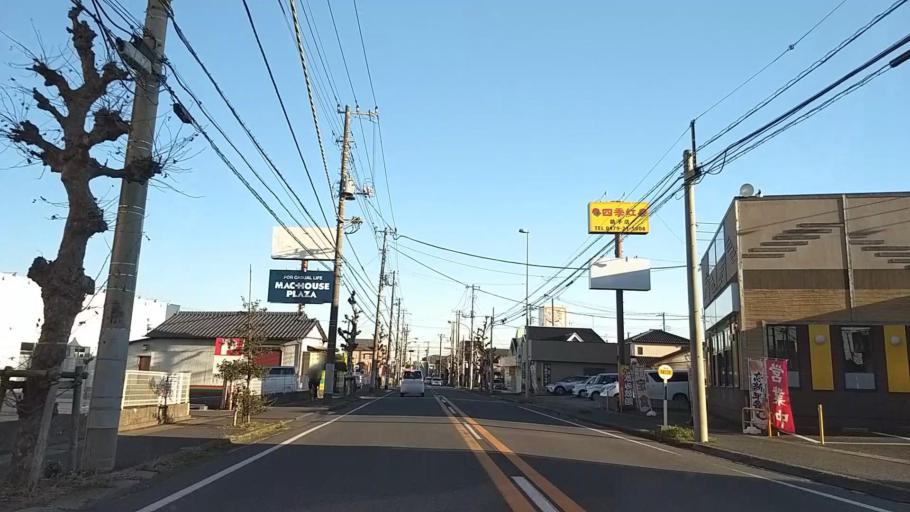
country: JP
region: Chiba
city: Hasaki
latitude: 35.7356
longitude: 140.8082
